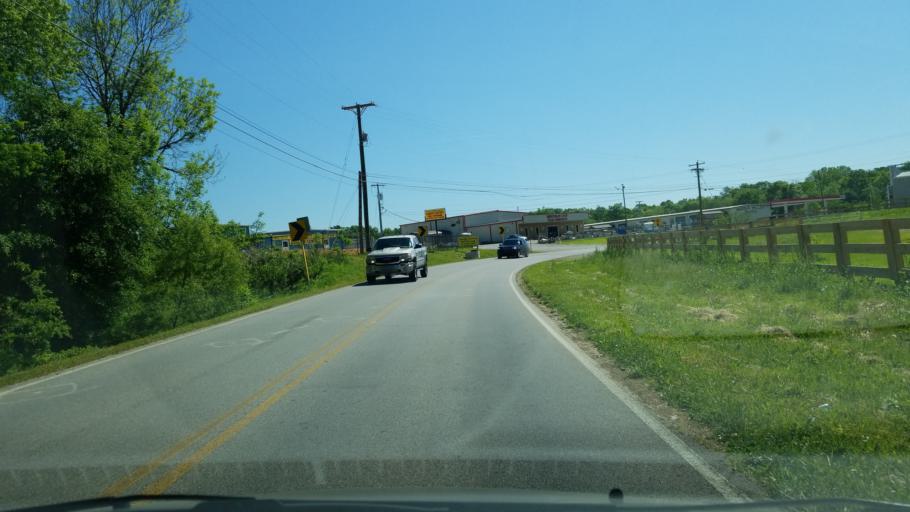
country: US
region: Tennessee
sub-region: Hamilton County
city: Middle Valley
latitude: 35.1735
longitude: -85.2090
